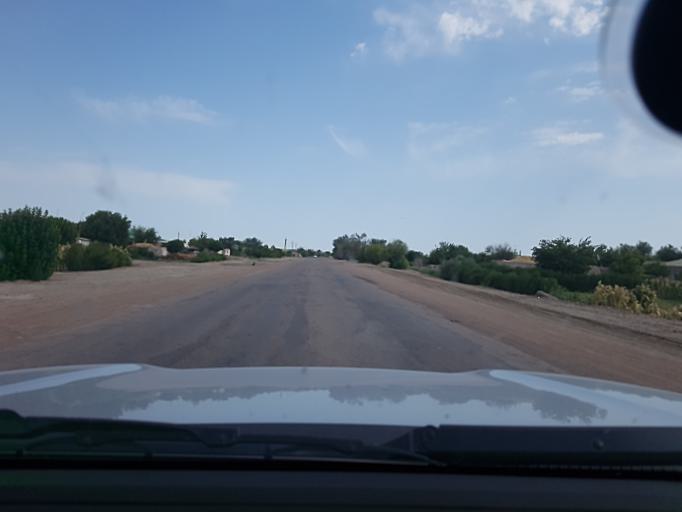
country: TM
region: Dasoguz
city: Boldumsaz
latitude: 42.0201
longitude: 59.8401
